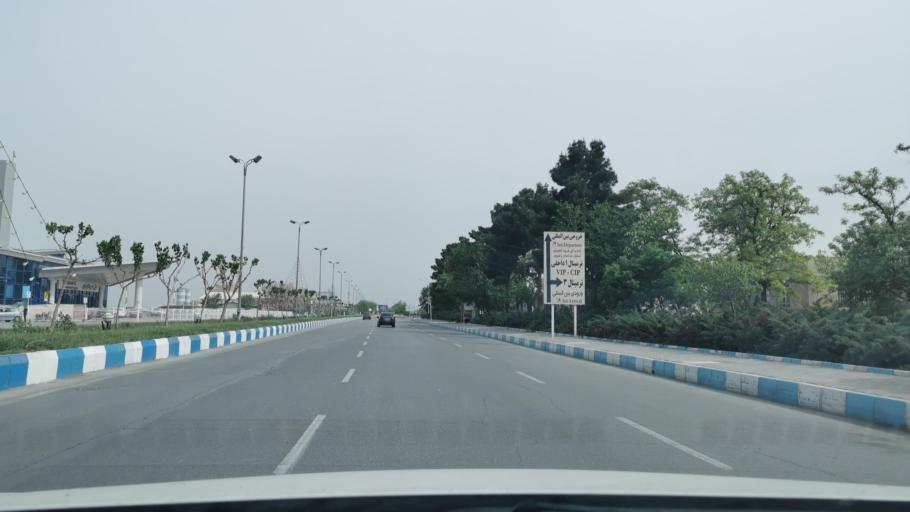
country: IR
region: Razavi Khorasan
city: Mashhad
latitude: 36.2344
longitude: 59.6323
